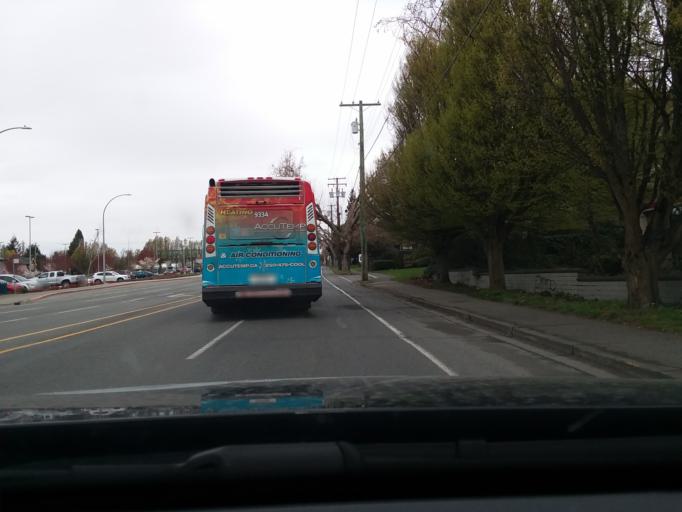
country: CA
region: British Columbia
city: Oak Bay
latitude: 48.4464
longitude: -123.3332
